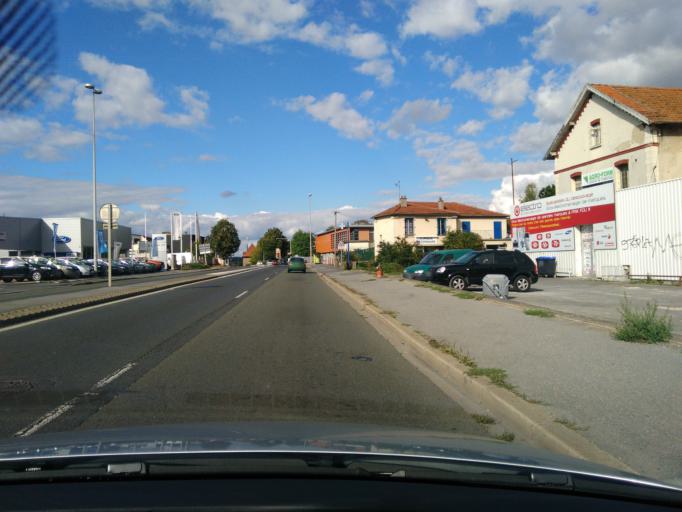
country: FR
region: Ile-de-France
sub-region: Departement de Seine-et-Marne
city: Meaux
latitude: 48.9474
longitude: 2.8799
